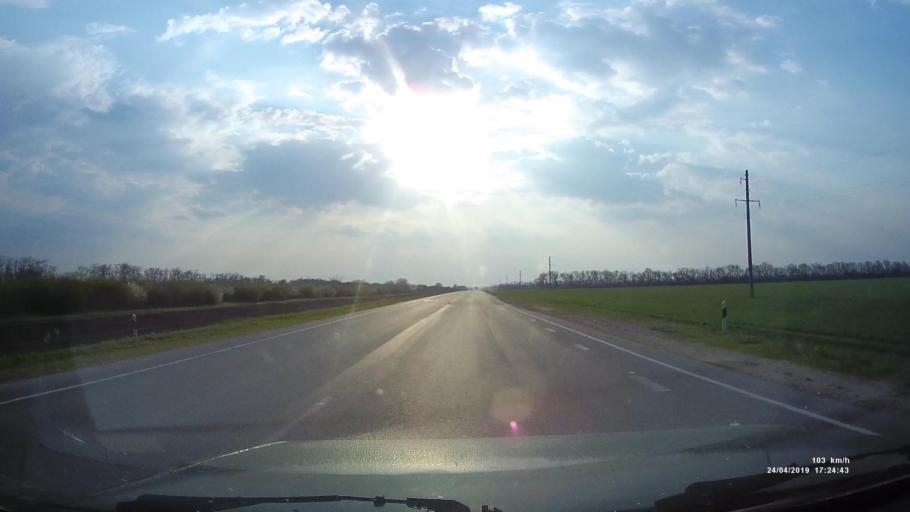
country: RU
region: Rostov
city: Gigant
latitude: 46.5243
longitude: 41.2559
